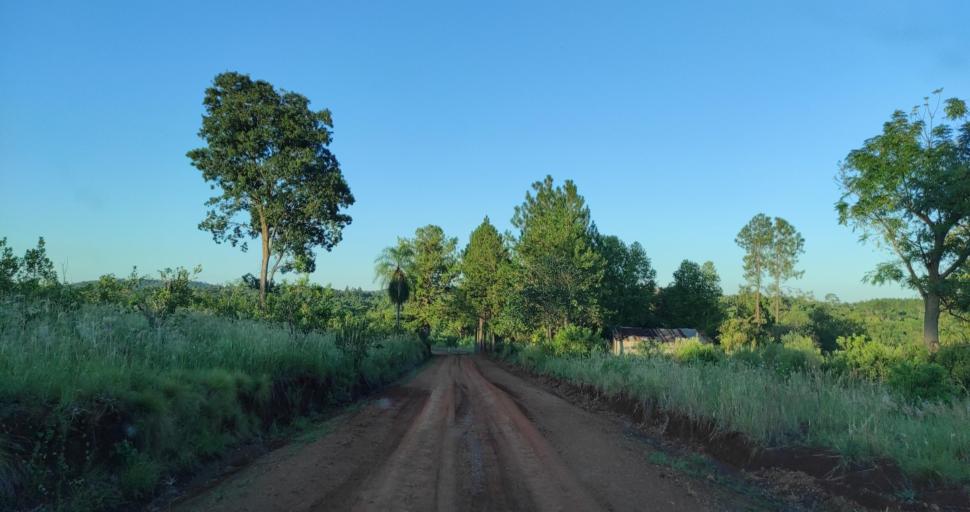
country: AR
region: Misiones
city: Gobernador Roca
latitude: -27.2165
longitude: -55.4133
